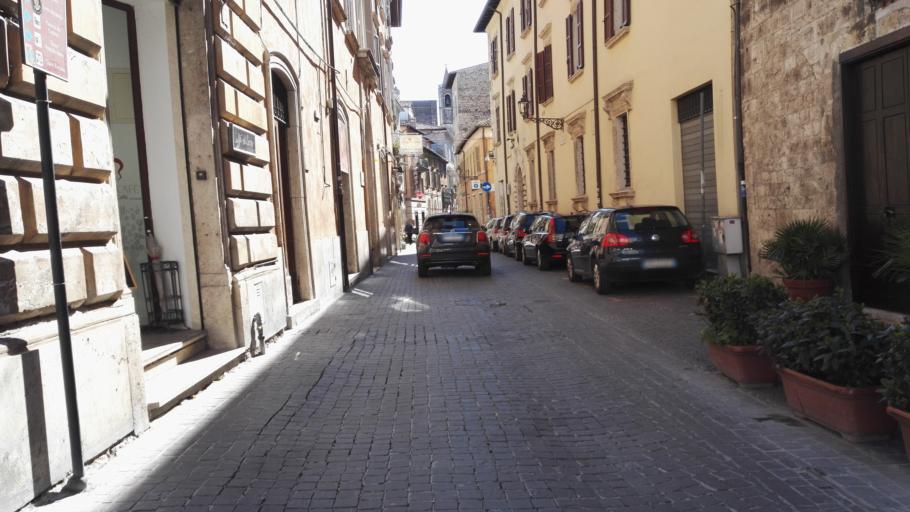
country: IT
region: The Marches
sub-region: Provincia di Ascoli Piceno
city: Ascoli Piceno
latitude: 42.8551
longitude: 13.5732
